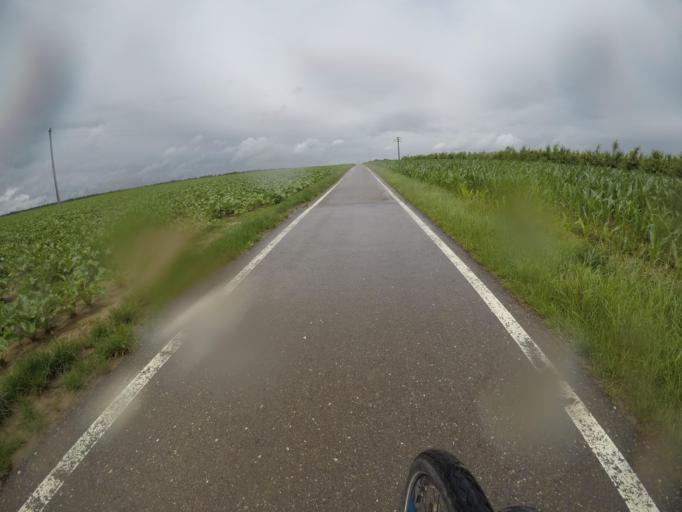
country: DE
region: Baden-Wuerttemberg
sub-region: Regierungsbezirk Stuttgart
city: Bondorf
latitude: 48.5316
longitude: 8.8220
